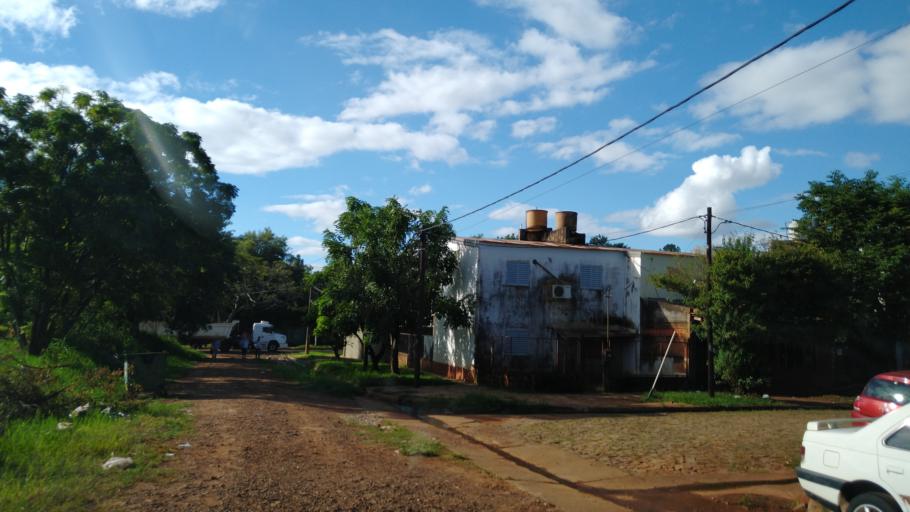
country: AR
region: Misiones
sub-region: Departamento de Capital
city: Posadas
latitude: -27.3585
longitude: -55.9255
